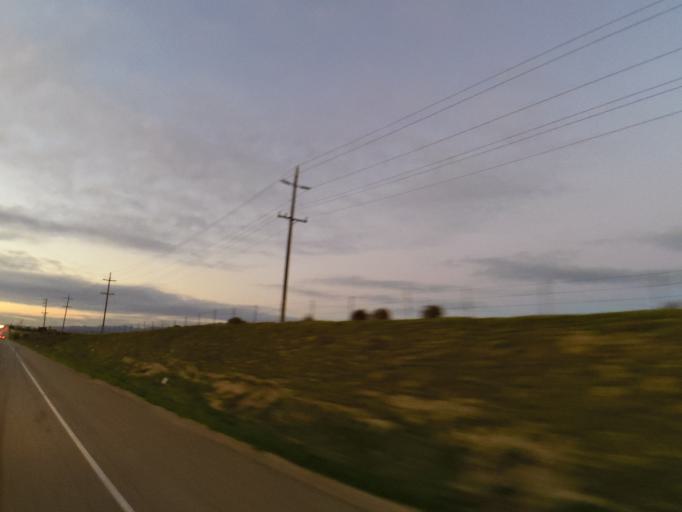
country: US
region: California
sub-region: Monterey County
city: Greenfield
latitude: 36.3463
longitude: -121.2614
